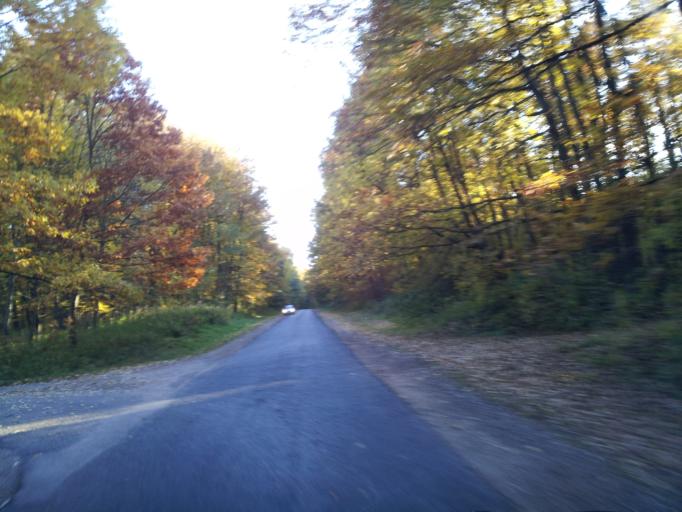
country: HU
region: Gyor-Moson-Sopron
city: Bakonyszentlaszlo
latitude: 47.3665
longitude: 17.8166
